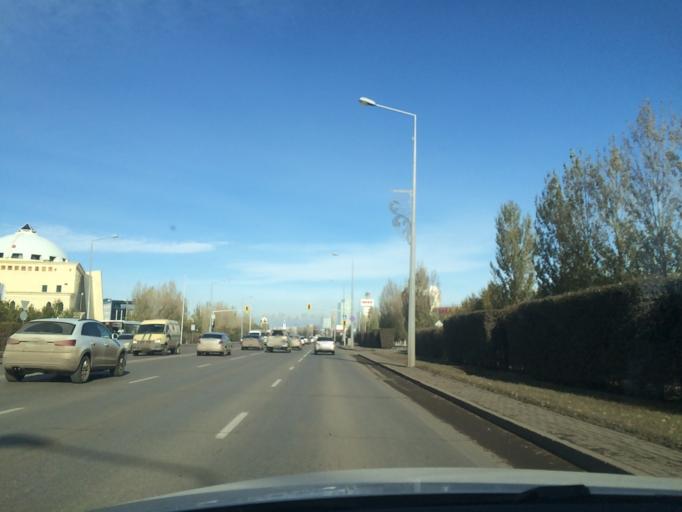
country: KZ
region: Astana Qalasy
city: Astana
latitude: 51.1426
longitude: 71.4110
